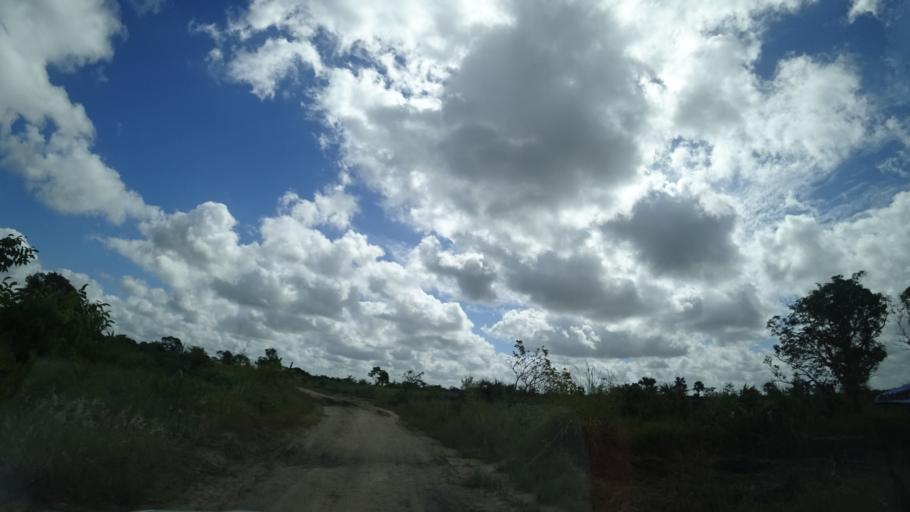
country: MZ
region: Sofala
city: Dondo
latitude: -19.3851
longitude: 34.5927
